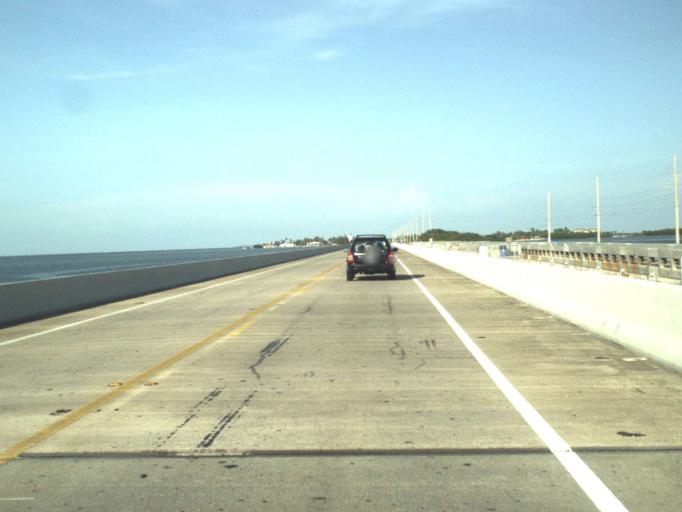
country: US
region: Florida
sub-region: Monroe County
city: Marathon
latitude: 24.7822
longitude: -80.9092
